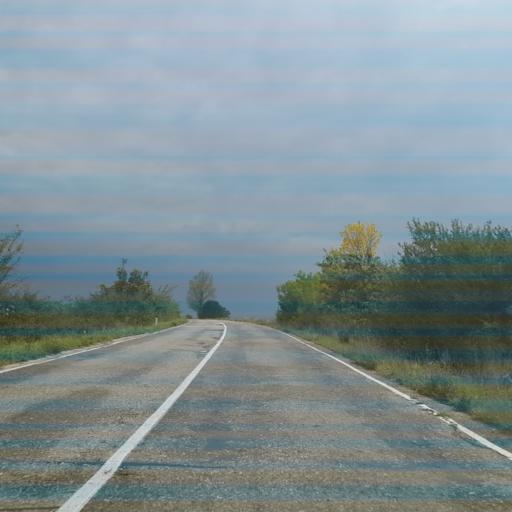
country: RS
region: Central Serbia
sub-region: Nisavski Okrug
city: Razanj
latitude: 43.6374
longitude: 21.5586
